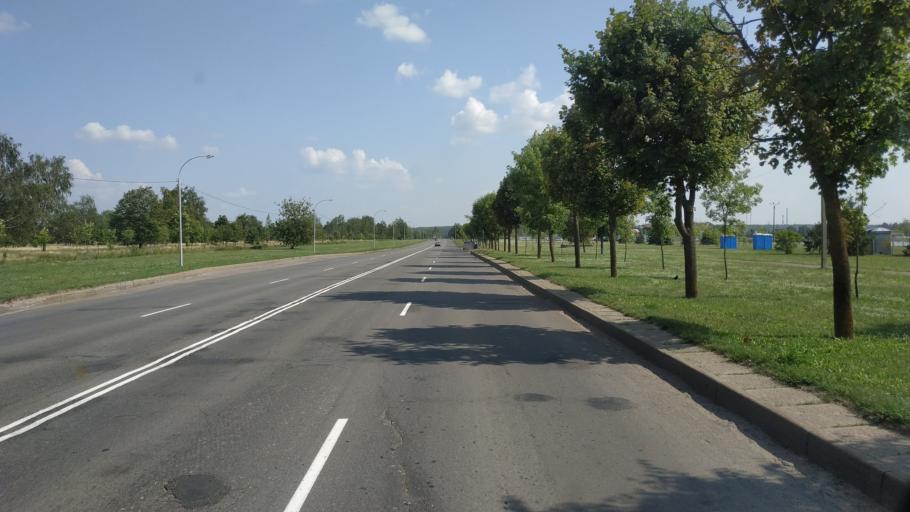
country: BY
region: Mogilev
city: Buynichy
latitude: 53.8628
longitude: 30.3208
